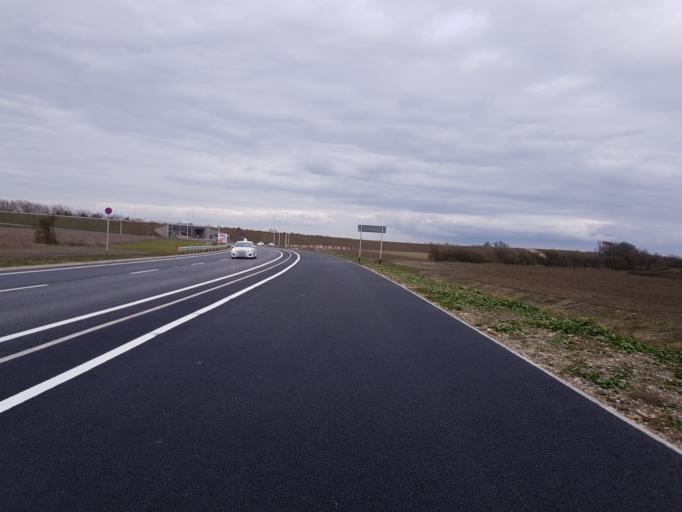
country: GB
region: England
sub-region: Cambridgeshire
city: Girton
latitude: 52.2362
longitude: 0.0588
